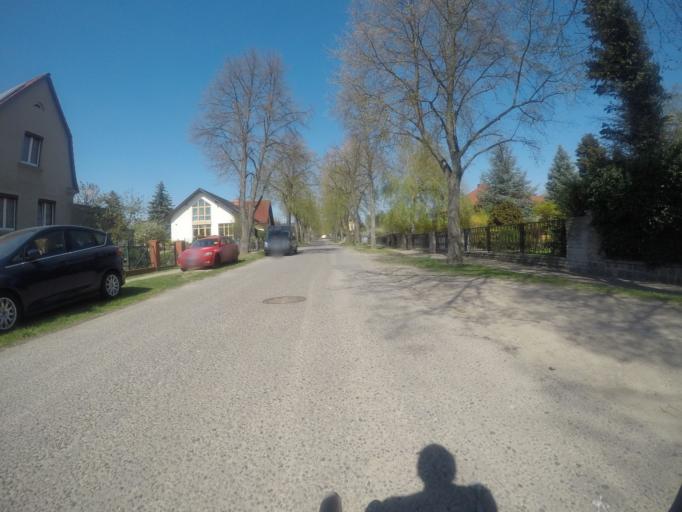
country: DE
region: Brandenburg
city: Bernau bei Berlin
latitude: 52.6842
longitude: 13.5897
